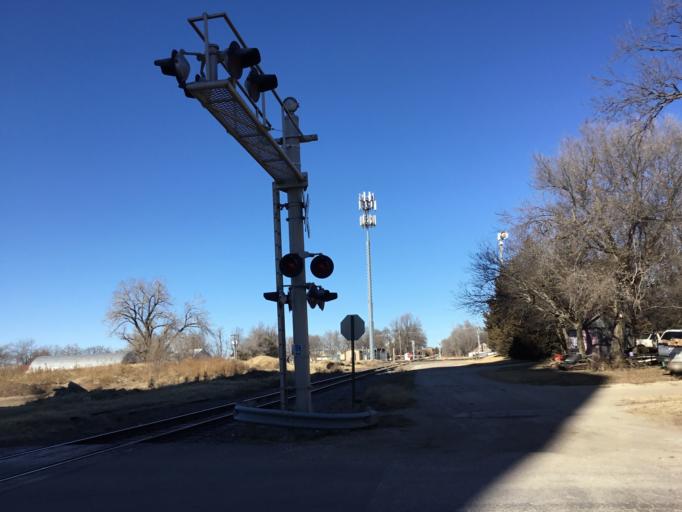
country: US
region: Kansas
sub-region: McPherson County
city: McPherson
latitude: 38.3714
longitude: -97.6722
